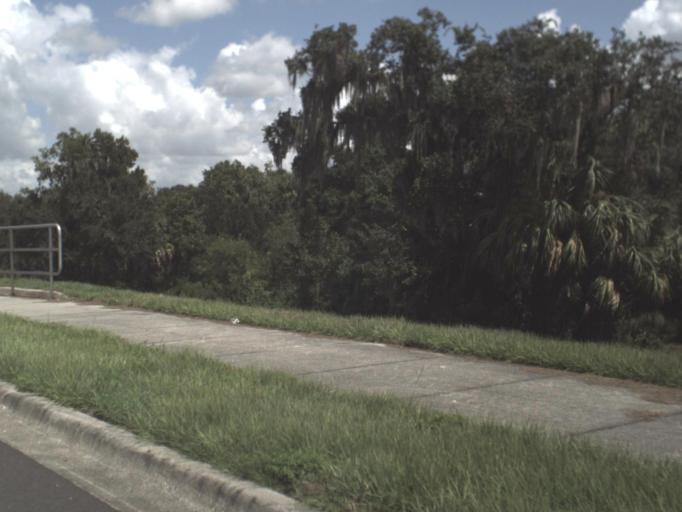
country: US
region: Florida
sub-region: Hardee County
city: Zolfo Springs
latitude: 27.5036
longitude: -81.7997
